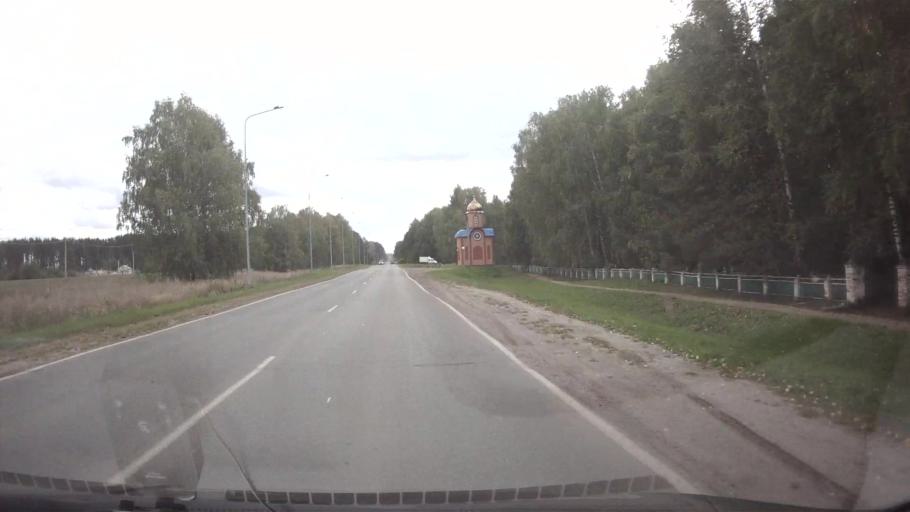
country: RU
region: Mariy-El
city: Kuzhener
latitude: 56.9941
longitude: 48.7427
